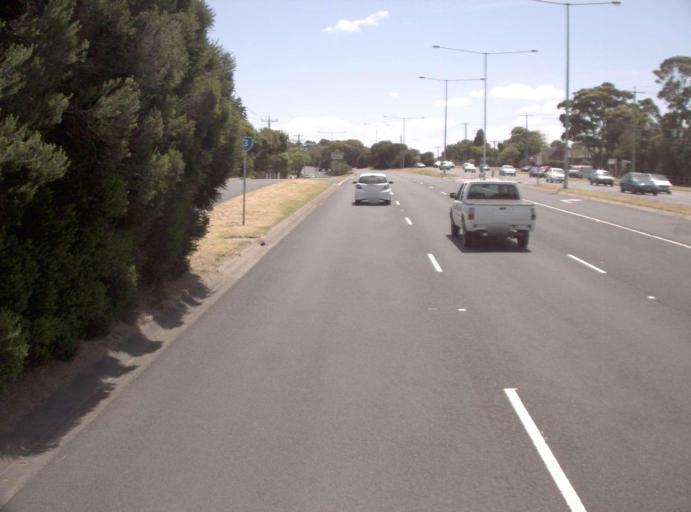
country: AU
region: Victoria
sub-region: Kingston
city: Mordialloc
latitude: -37.9967
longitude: 145.0835
